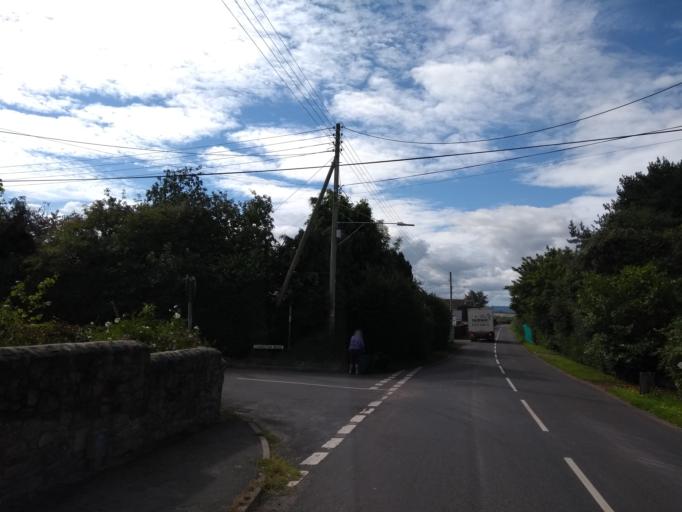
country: GB
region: England
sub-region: Somerset
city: Creech Saint Michael
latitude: 51.0380
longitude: -3.0318
